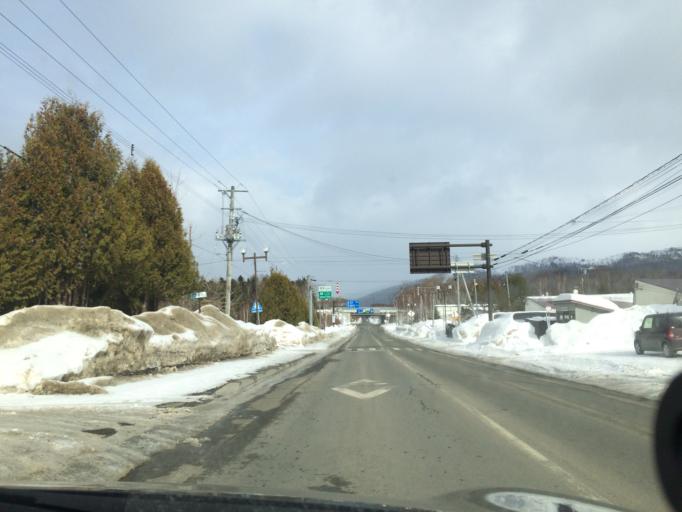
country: JP
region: Hokkaido
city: Shimo-furano
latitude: 43.0423
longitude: 142.6558
